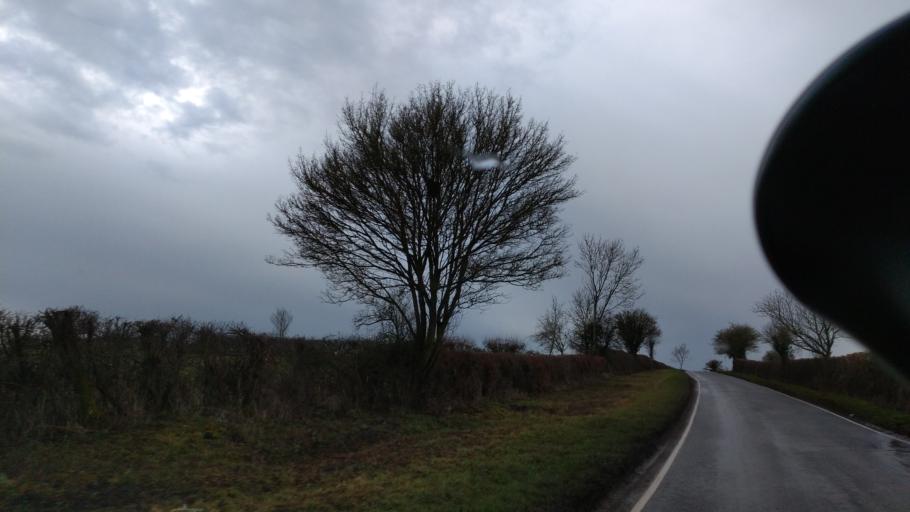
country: GB
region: England
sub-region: Borough of Swindon
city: Highworth
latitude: 51.6112
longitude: -1.7076
